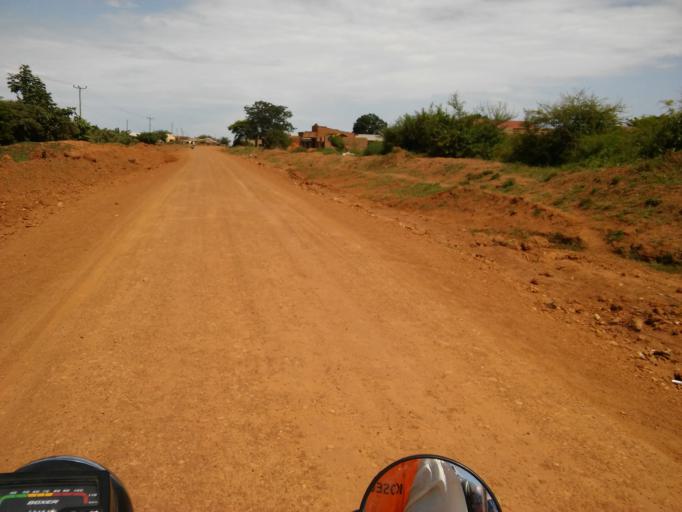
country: UG
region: Eastern Region
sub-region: Kumi District
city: Kumi
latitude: 1.4731
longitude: 33.8717
